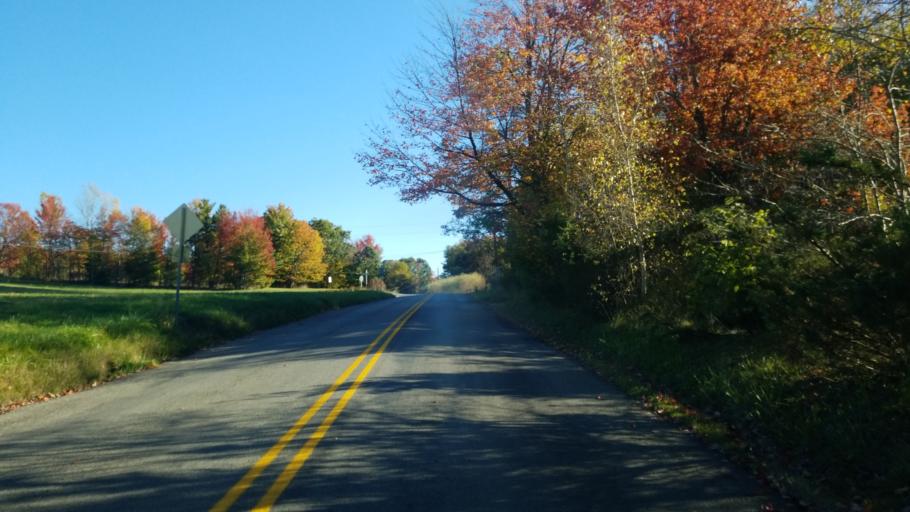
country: US
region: Pennsylvania
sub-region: Indiana County
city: Johnsonburg
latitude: 40.9109
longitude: -78.8771
